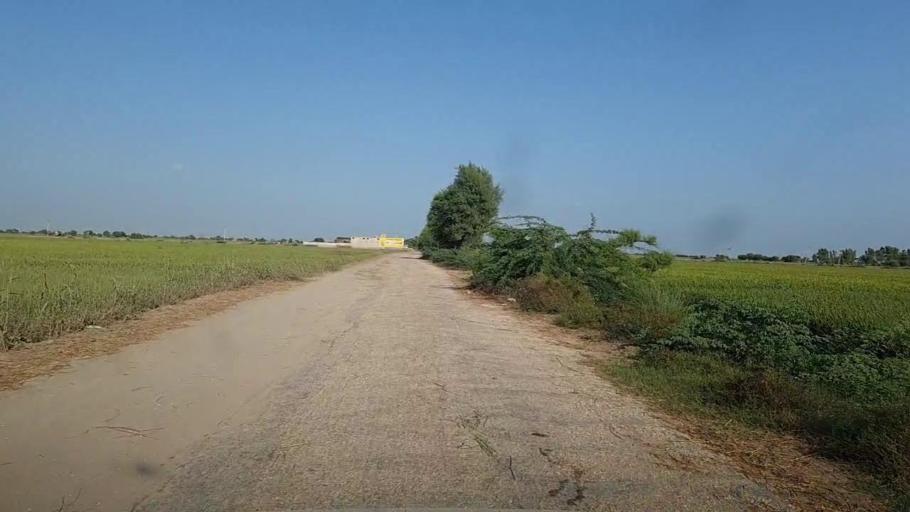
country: PK
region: Sindh
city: Kario
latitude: 24.5997
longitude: 68.5329
